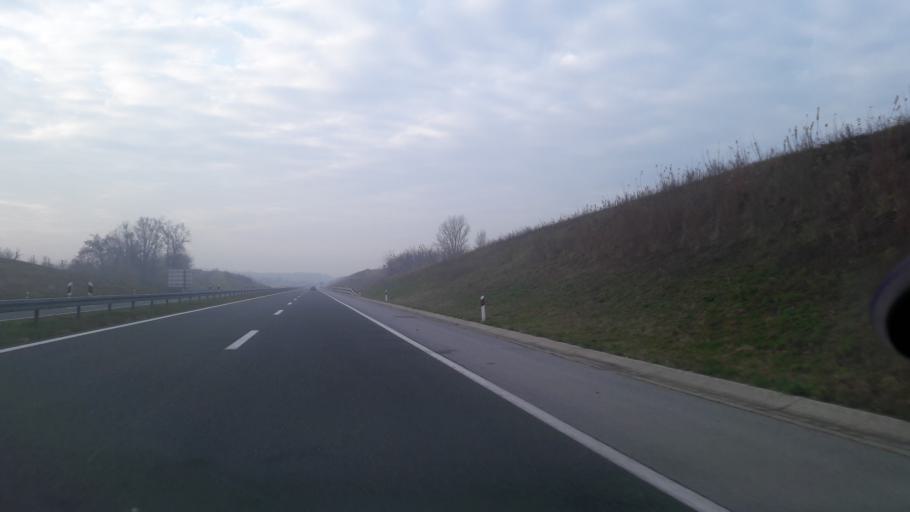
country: HR
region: Osjecko-Baranjska
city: Piskorevci
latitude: 45.2984
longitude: 18.3610
